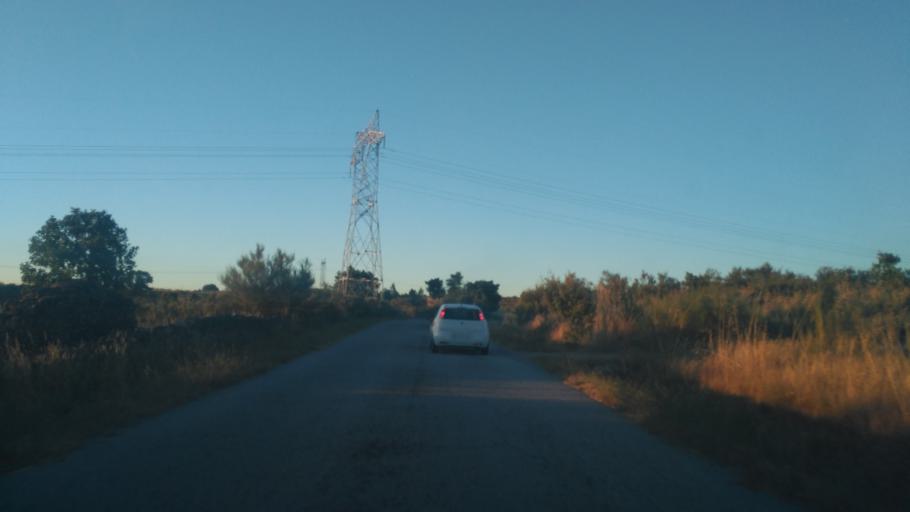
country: ES
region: Castille and Leon
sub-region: Provincia de Salamanca
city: Aldeadavila de la Ribera
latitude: 41.2026
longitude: -6.6442
